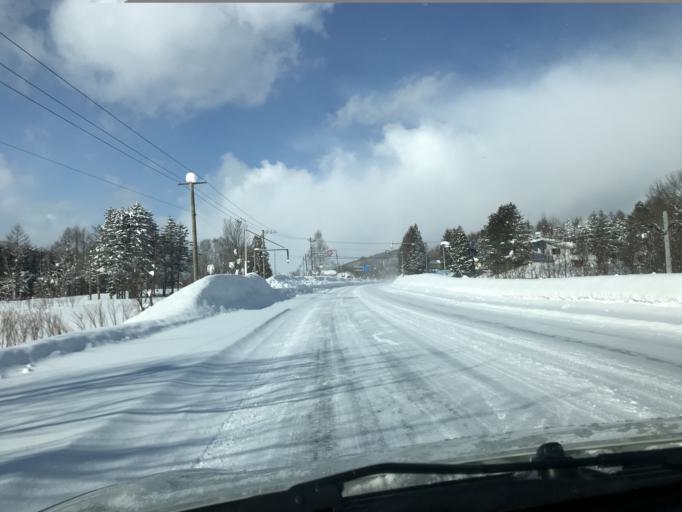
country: JP
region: Hokkaido
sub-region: Asahikawa-shi
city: Asahikawa
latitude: 43.9268
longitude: 142.4743
